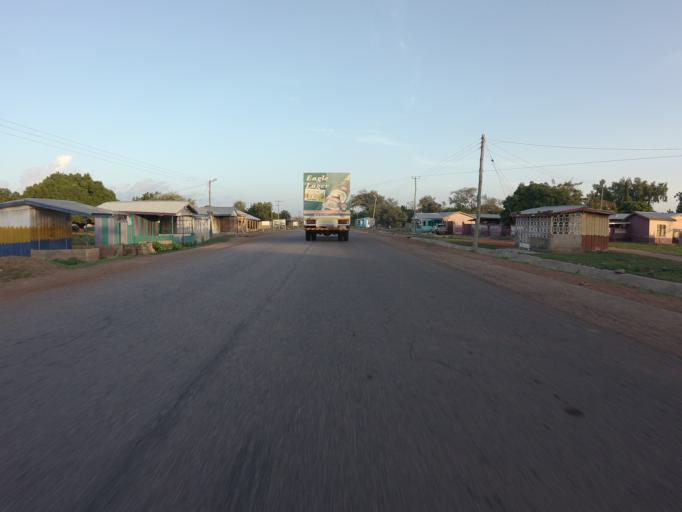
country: GH
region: Upper East
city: Navrongo
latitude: 10.9615
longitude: -1.0992
